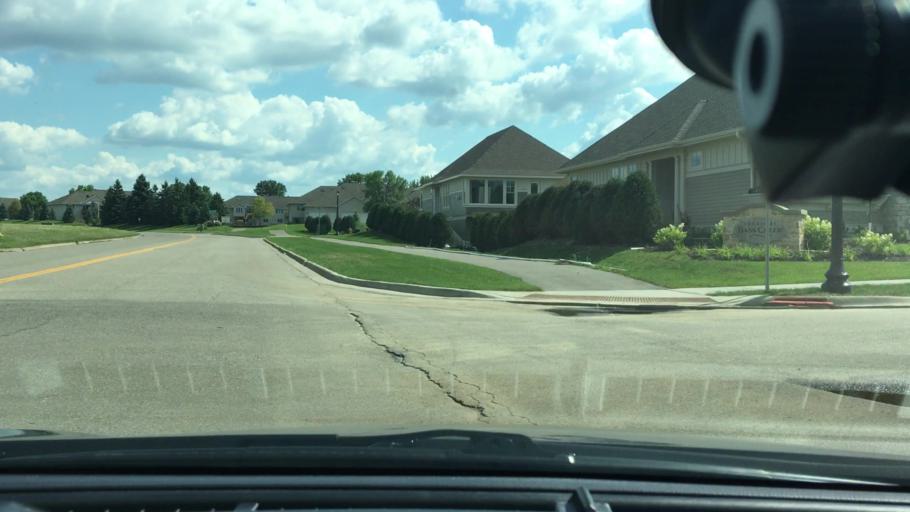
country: US
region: Minnesota
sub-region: Hennepin County
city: New Hope
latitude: 45.0569
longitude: -93.4080
